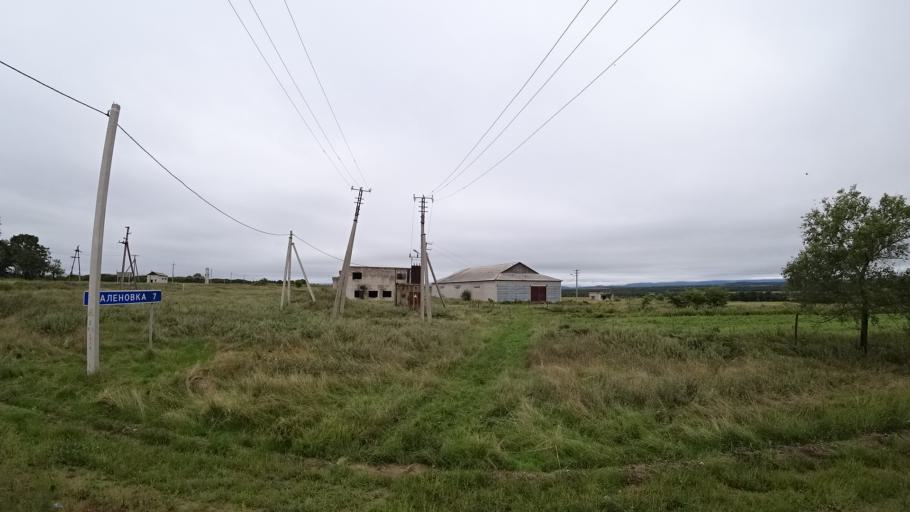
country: RU
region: Primorskiy
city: Monastyrishche
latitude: 44.0772
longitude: 132.5887
